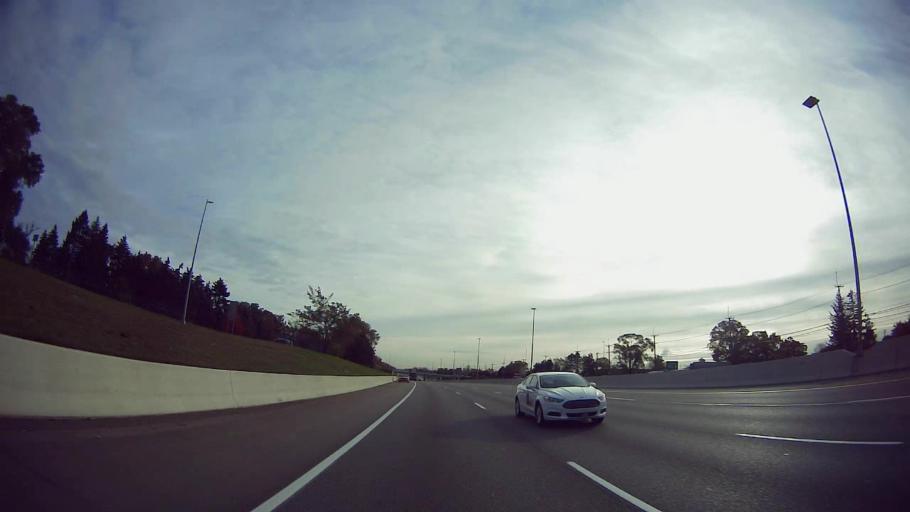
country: US
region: Michigan
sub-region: Wayne County
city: Plymouth
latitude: 42.3821
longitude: -83.4188
